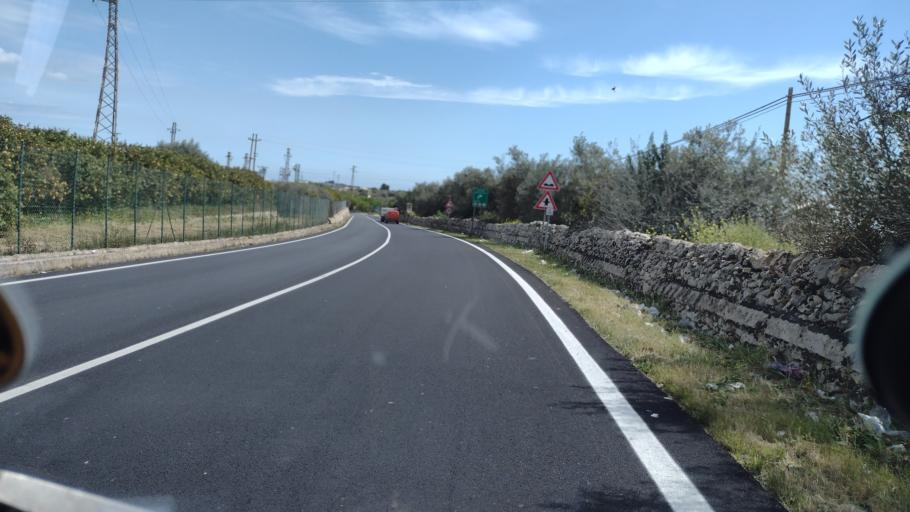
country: IT
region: Sicily
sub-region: Provincia di Siracusa
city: Noto
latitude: 36.8768
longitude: 15.0492
